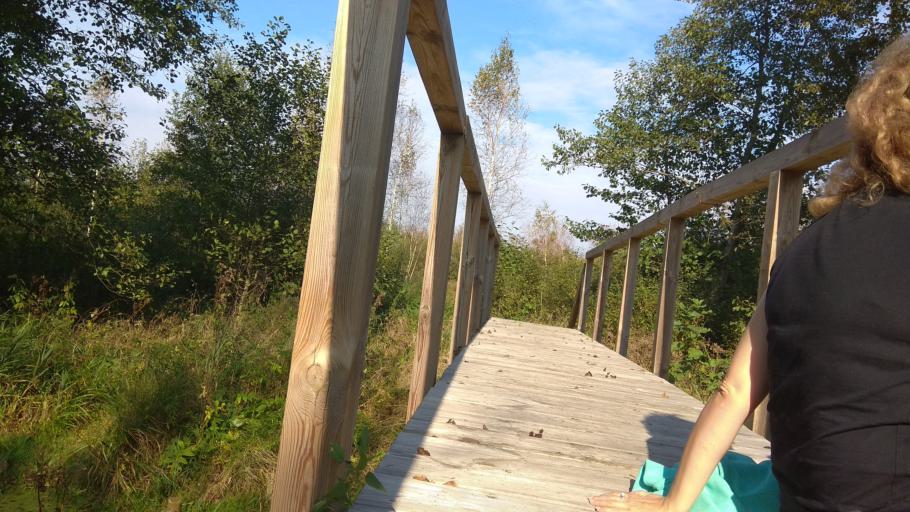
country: PL
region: Podlasie
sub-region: Powiat moniecki
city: Goniadz
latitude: 53.5398
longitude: 22.6994
